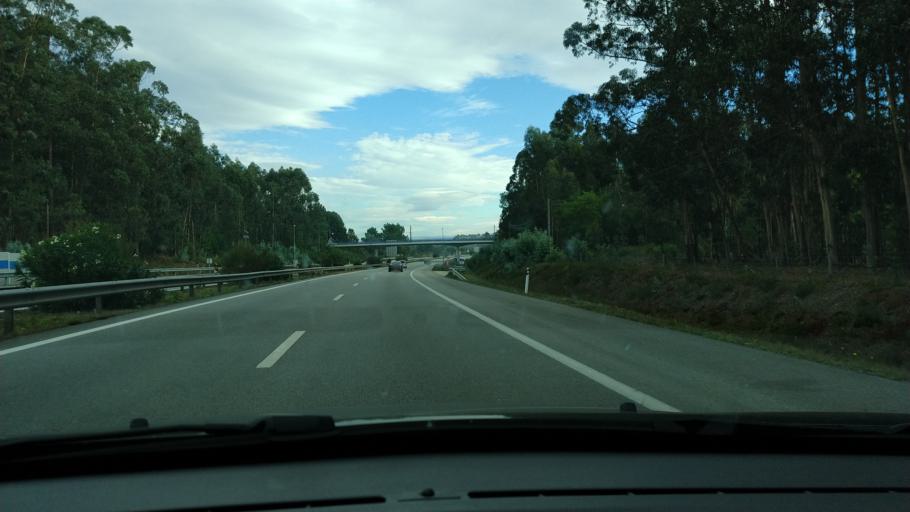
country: PT
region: Aveiro
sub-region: Aveiro
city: Eixo
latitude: 40.6656
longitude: -8.5900
